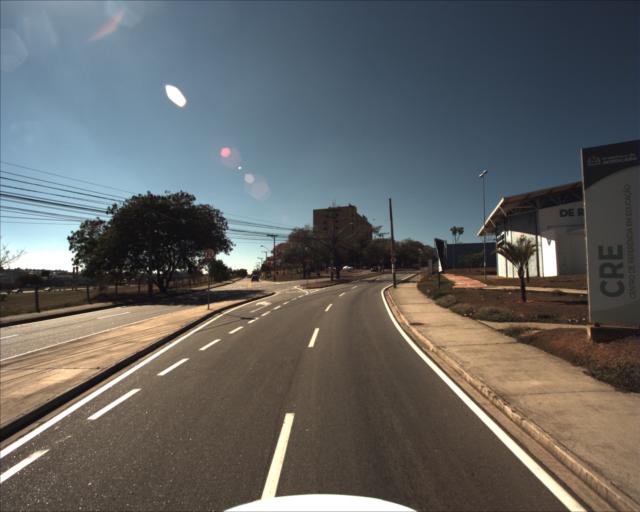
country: BR
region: Sao Paulo
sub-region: Sorocaba
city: Sorocaba
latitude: -23.4779
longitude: -47.4378
